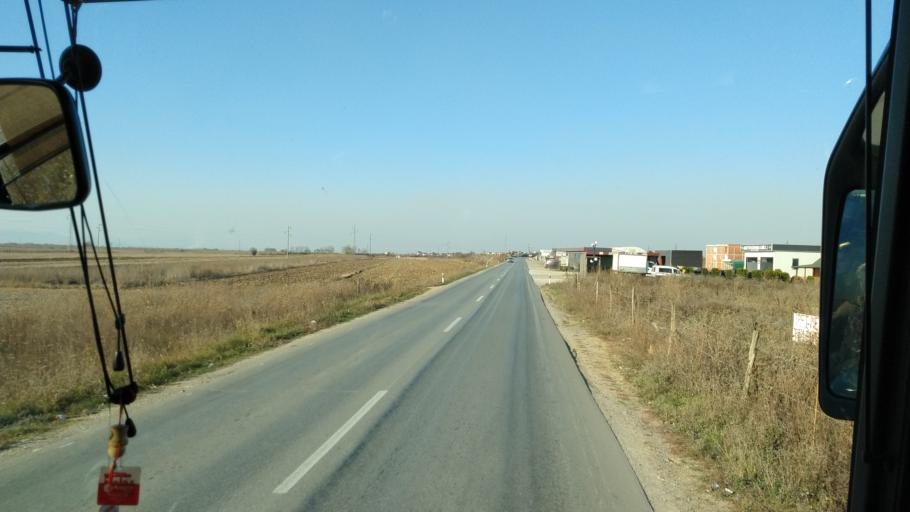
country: XK
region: Pristina
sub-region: Lipjan
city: Lipljan
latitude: 42.5215
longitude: 21.1122
